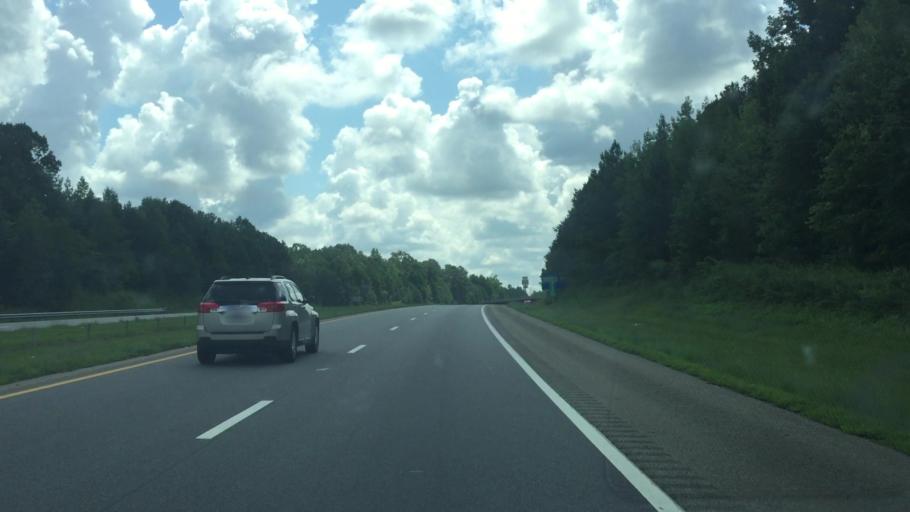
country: US
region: North Carolina
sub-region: Richmond County
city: Cordova
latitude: 34.9169
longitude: -79.8003
